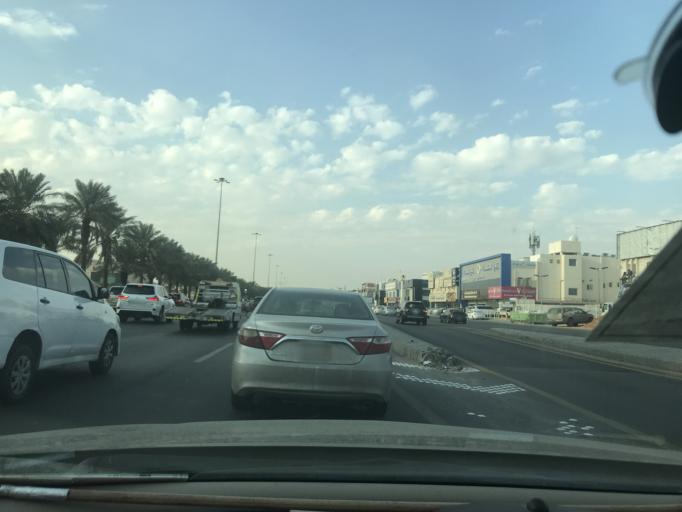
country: SA
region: Ar Riyad
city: Riyadh
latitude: 24.7447
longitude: 46.7467
